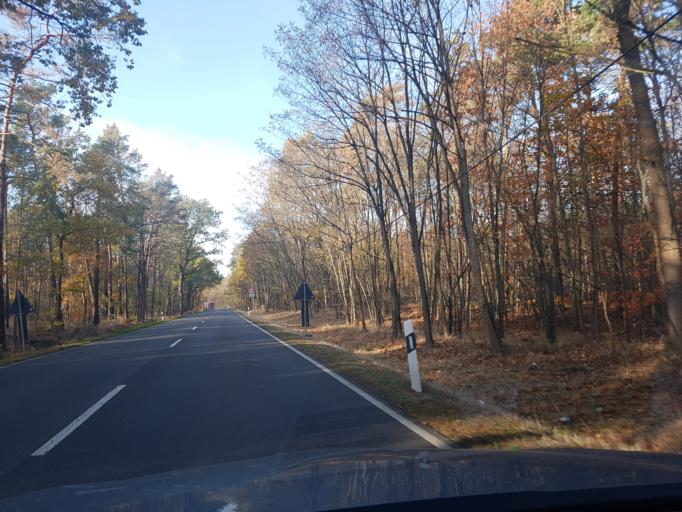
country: DE
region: Brandenburg
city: Falkenberg
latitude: 51.5436
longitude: 13.2606
